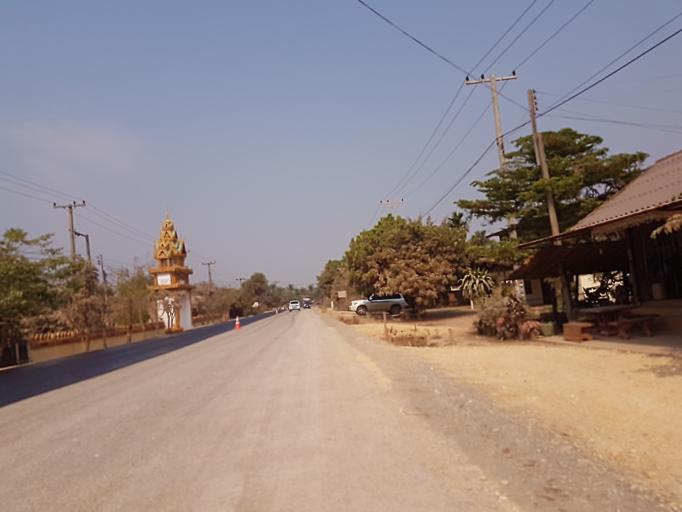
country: TH
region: Nong Khai
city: Nong Khai
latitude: 17.9337
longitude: 102.7803
